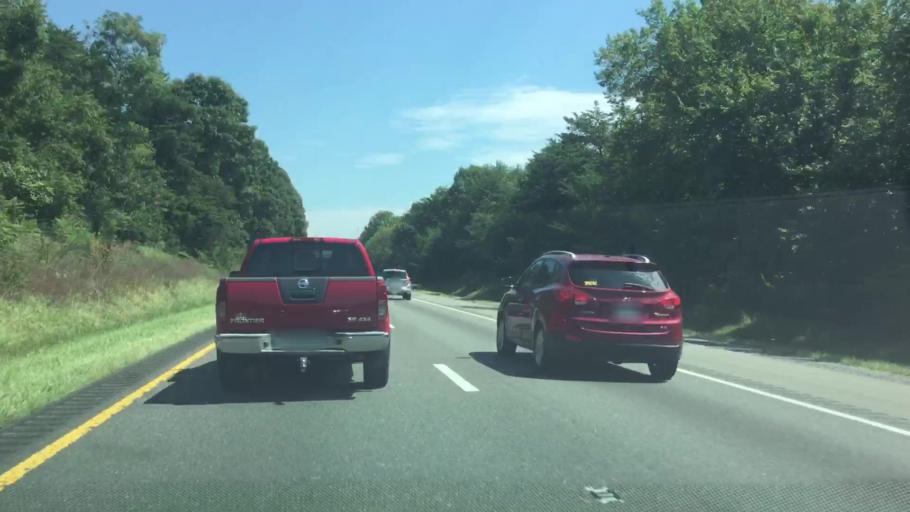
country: US
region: Virginia
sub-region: City of Salem
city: Salem
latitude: 37.2887
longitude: -80.1140
